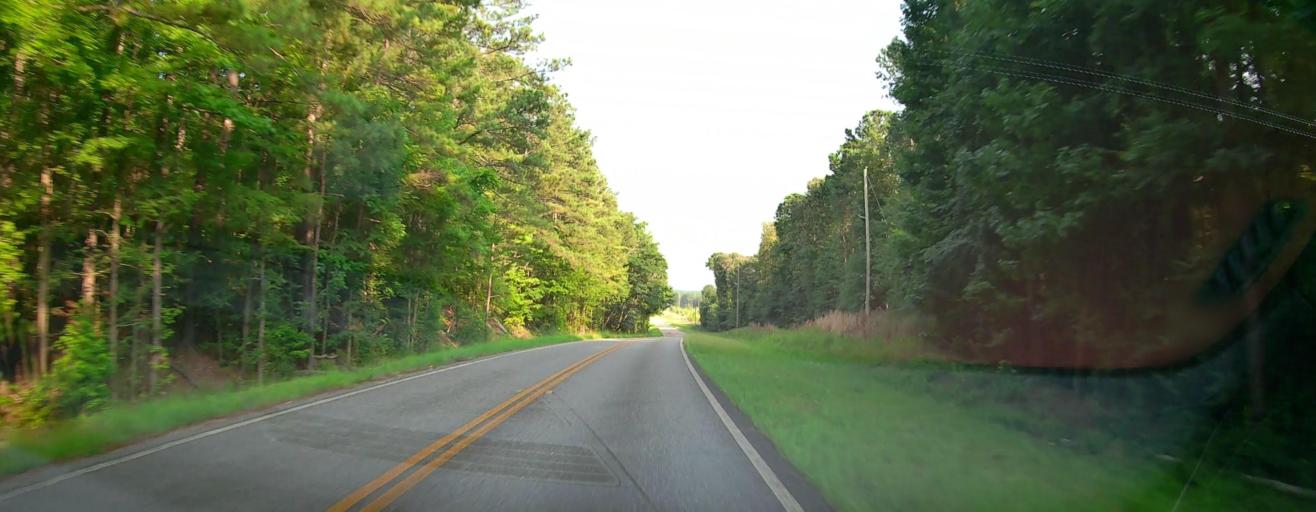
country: US
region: Georgia
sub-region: Monroe County
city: Forsyth
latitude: 33.1069
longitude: -83.7773
